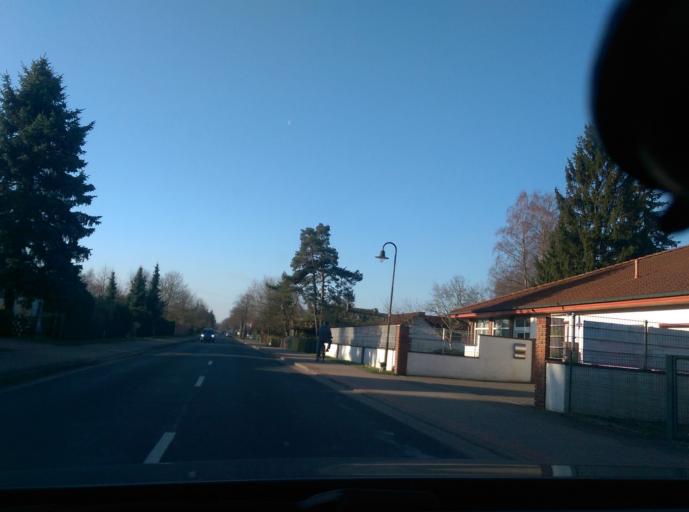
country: DE
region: Lower Saxony
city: Lindwedel
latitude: 52.6159
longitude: 9.6884
